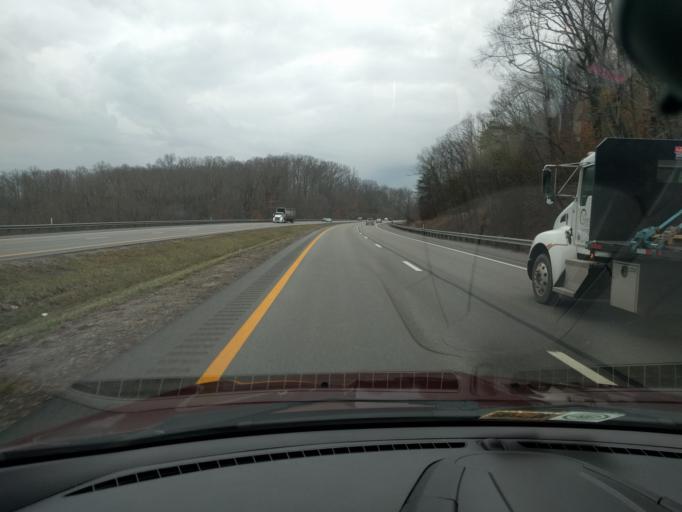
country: US
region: West Virginia
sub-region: Wood County
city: Williamstown
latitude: 39.3500
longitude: -81.4486
